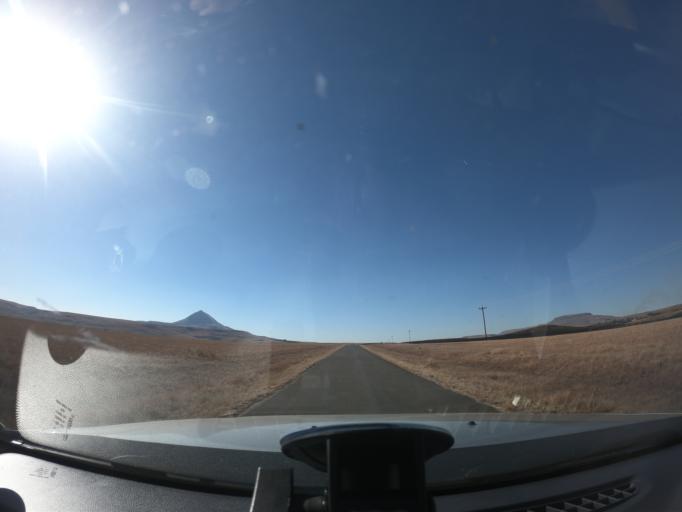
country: ZA
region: KwaZulu-Natal
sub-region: uMgungundlovu District Municipality
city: Impendle
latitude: -29.3876
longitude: 29.7252
